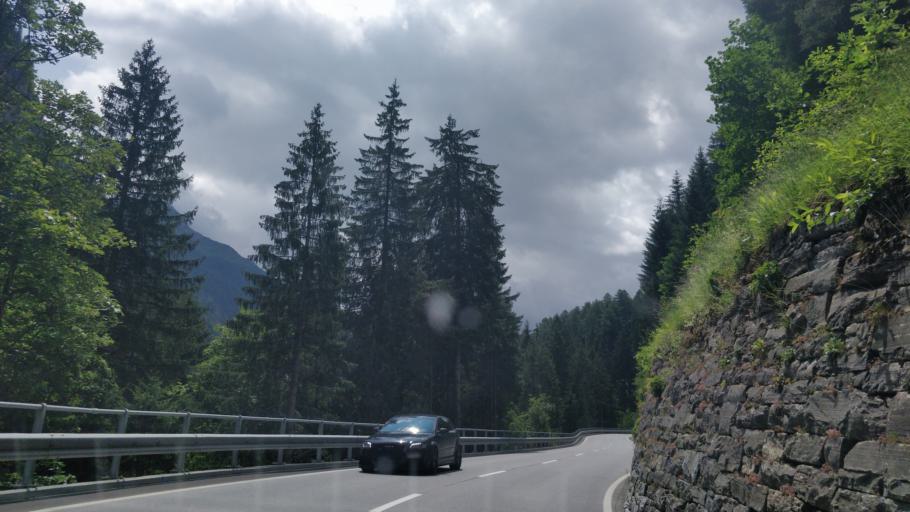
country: CH
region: Grisons
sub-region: Hinterrhein District
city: Hinterrhein
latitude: 46.6384
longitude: 9.1867
